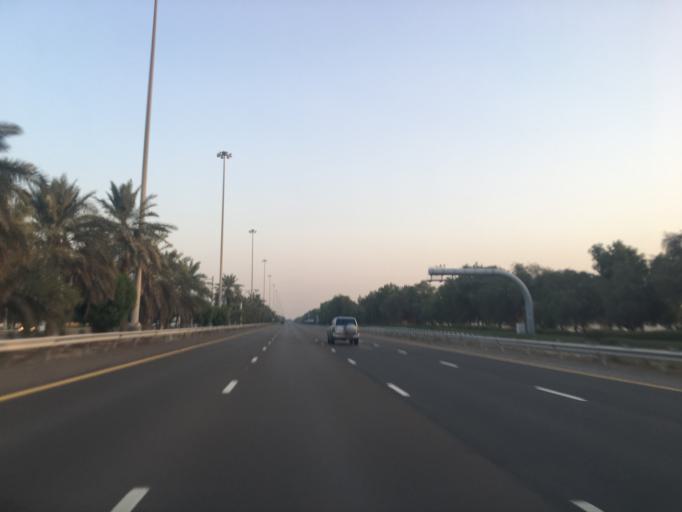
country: AE
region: Abu Dhabi
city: Abu Dhabi
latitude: 24.3322
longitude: 54.5827
